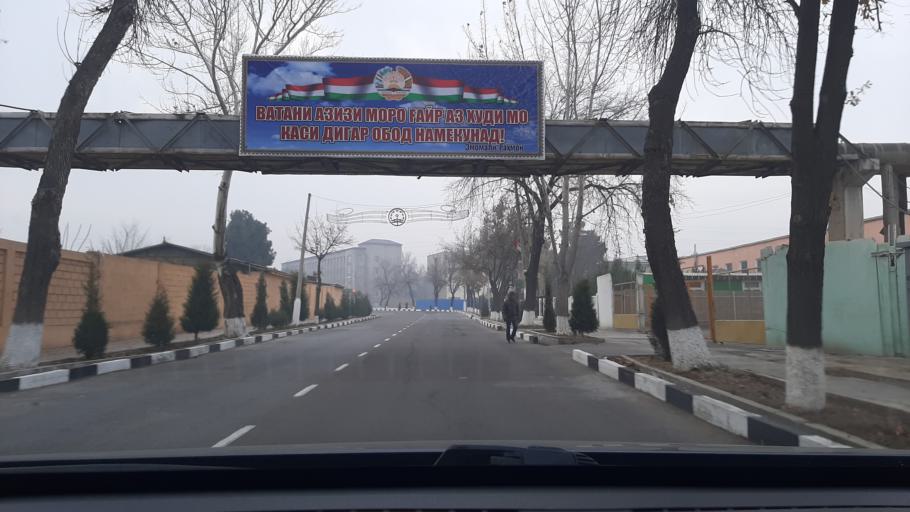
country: TJ
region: Viloyati Sughd
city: Chkalov
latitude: 40.2368
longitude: 69.6887
